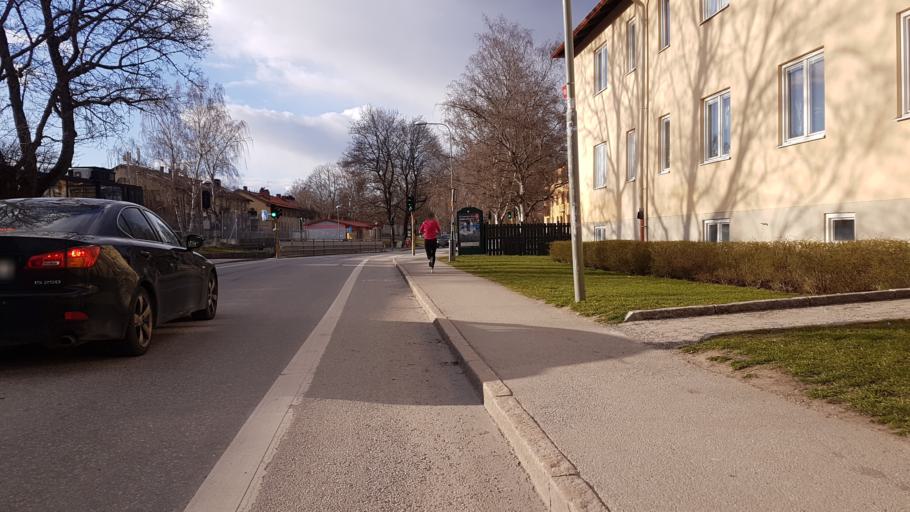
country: SE
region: Stockholm
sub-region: Stockholms Kommun
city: Arsta
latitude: 59.2892
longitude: 18.0707
